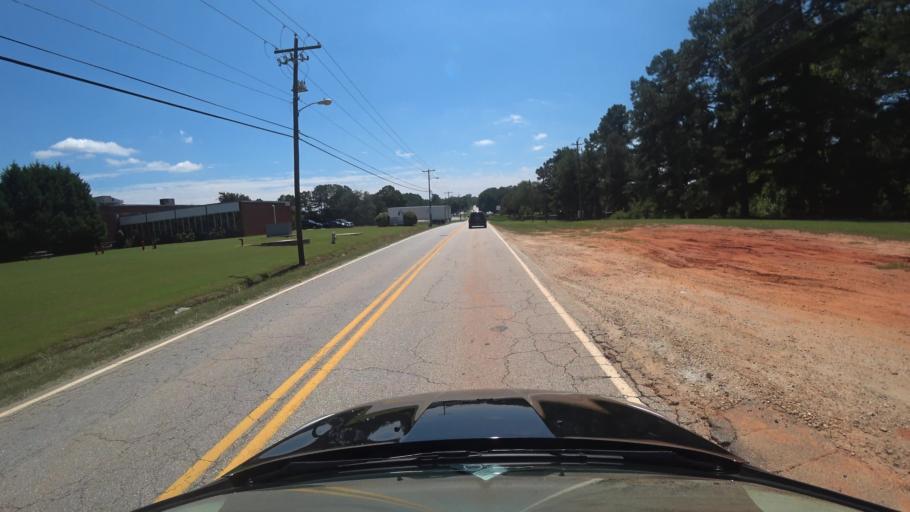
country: US
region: Georgia
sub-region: Newton County
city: Covington
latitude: 33.6115
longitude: -83.8378
